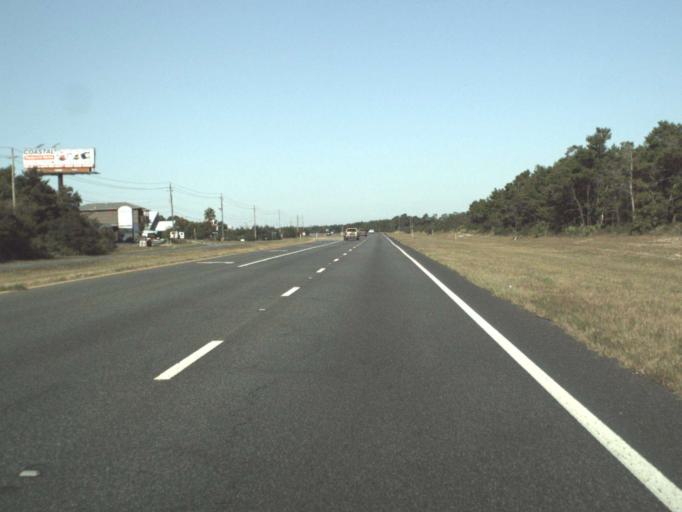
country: US
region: Florida
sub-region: Bay County
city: Laguna Beach
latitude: 30.2580
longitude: -85.9481
